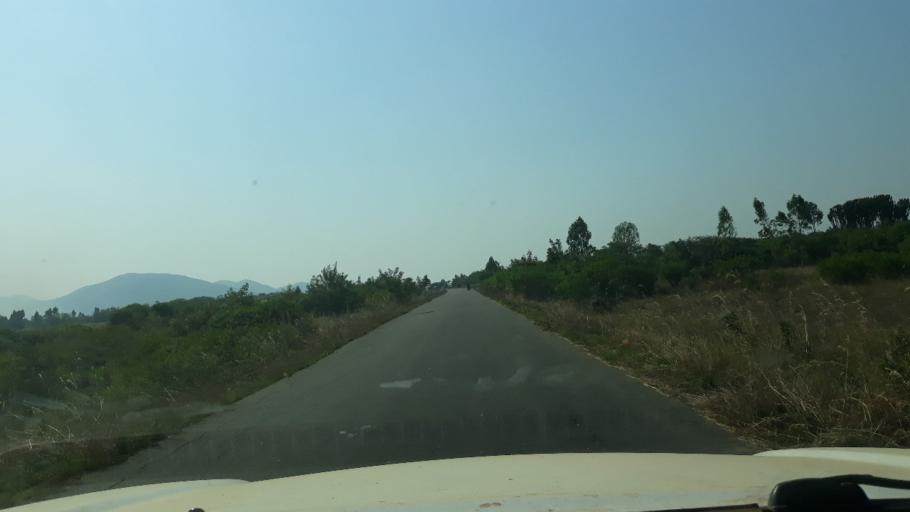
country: BI
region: Cibitoke
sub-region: Commune of Buganda
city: Buganda
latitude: -3.1538
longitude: 29.1476
